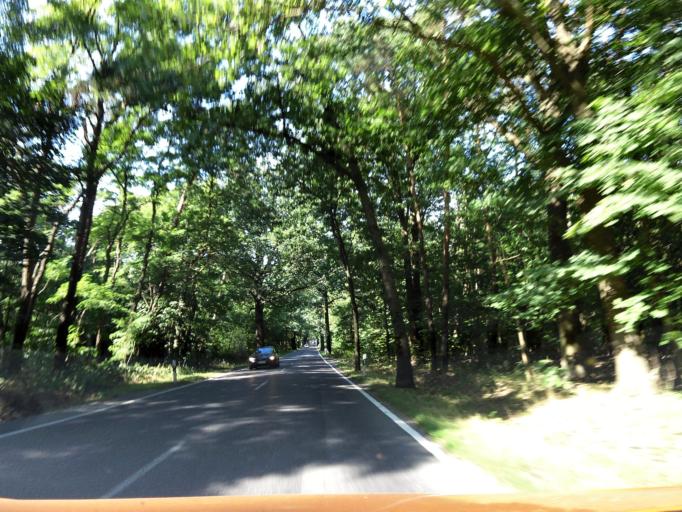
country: DE
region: Brandenburg
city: Teltow
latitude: 52.3677
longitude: 13.2653
